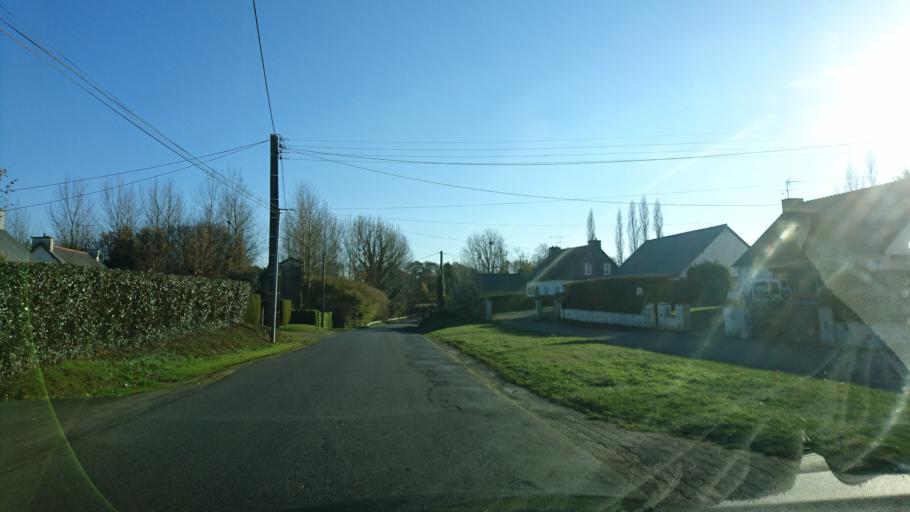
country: FR
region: Brittany
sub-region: Departement des Cotes-d'Armor
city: Pedernec
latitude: 48.5843
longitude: -3.2619
